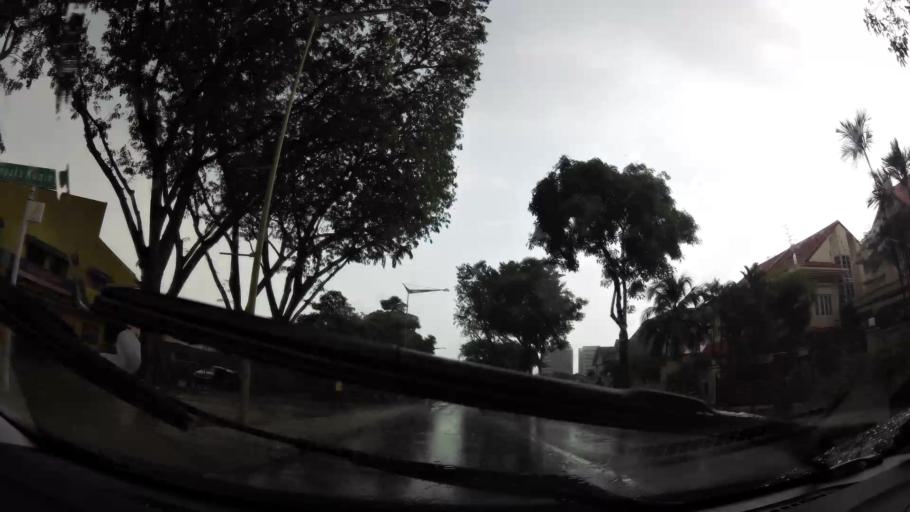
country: SG
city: Singapore
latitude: 1.3306
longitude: 103.9481
